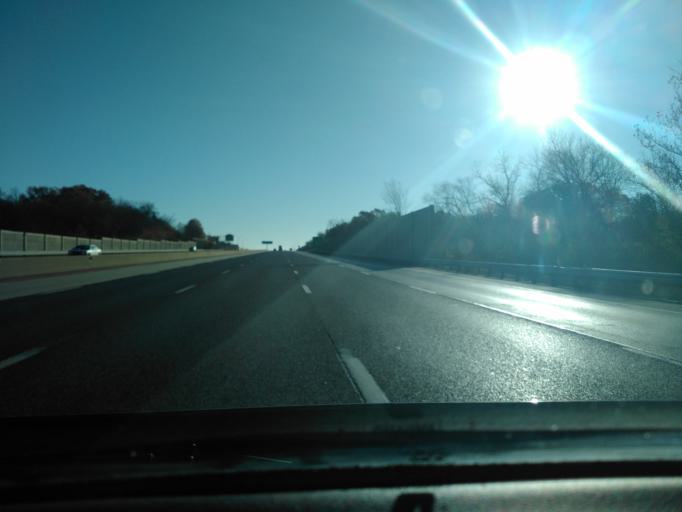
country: US
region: Missouri
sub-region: Saint Louis County
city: Concord
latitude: 38.5107
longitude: -90.3630
